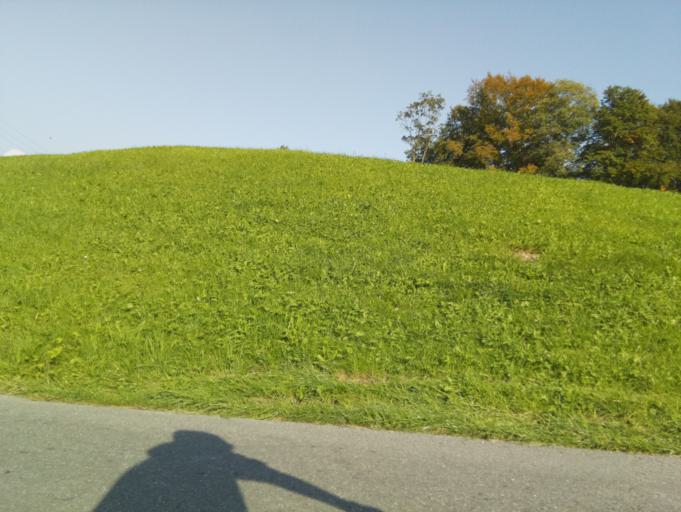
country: CH
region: Schwyz
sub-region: Bezirk March
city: Schubelbach
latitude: 47.1681
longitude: 8.8926
